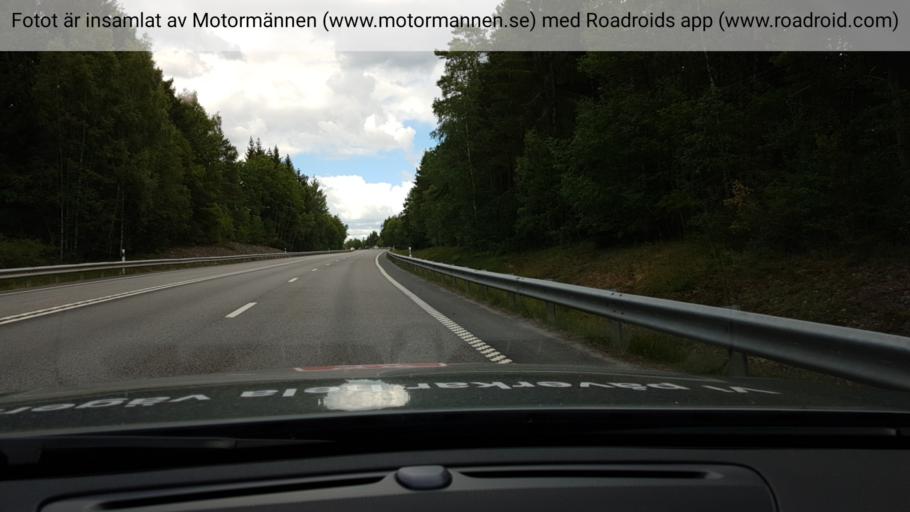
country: SE
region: Stockholm
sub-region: Lidingo
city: Brevik
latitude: 59.4357
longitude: 18.2196
